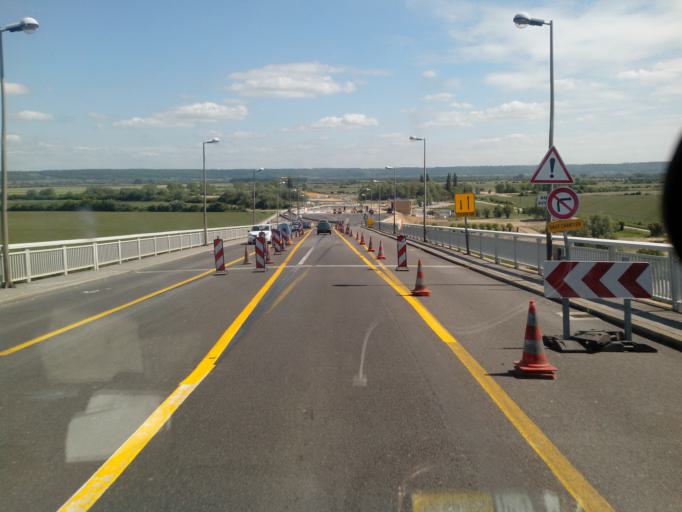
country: FR
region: Haute-Normandie
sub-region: Departement de la Seine-Maritime
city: Tancarville
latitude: 49.4668
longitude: 0.4708
